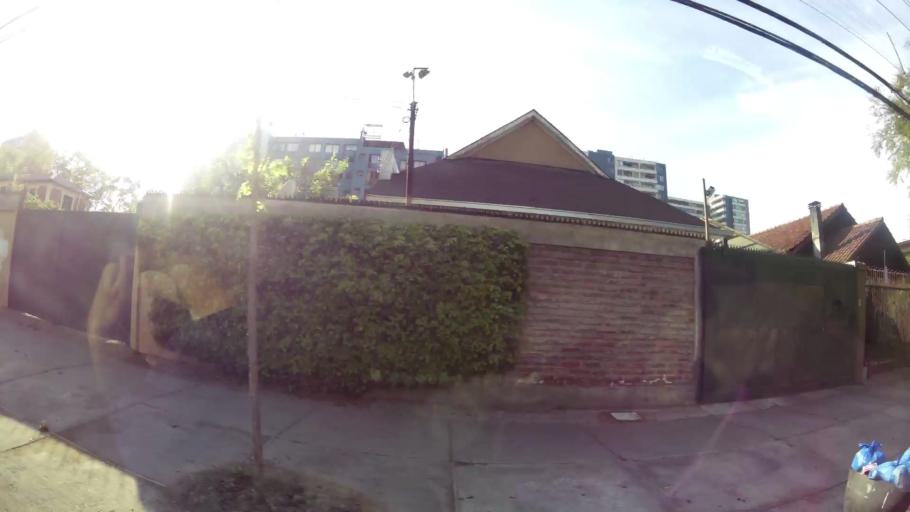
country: CL
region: Santiago Metropolitan
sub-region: Provincia de Santiago
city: Santiago
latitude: -33.5101
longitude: -70.6598
